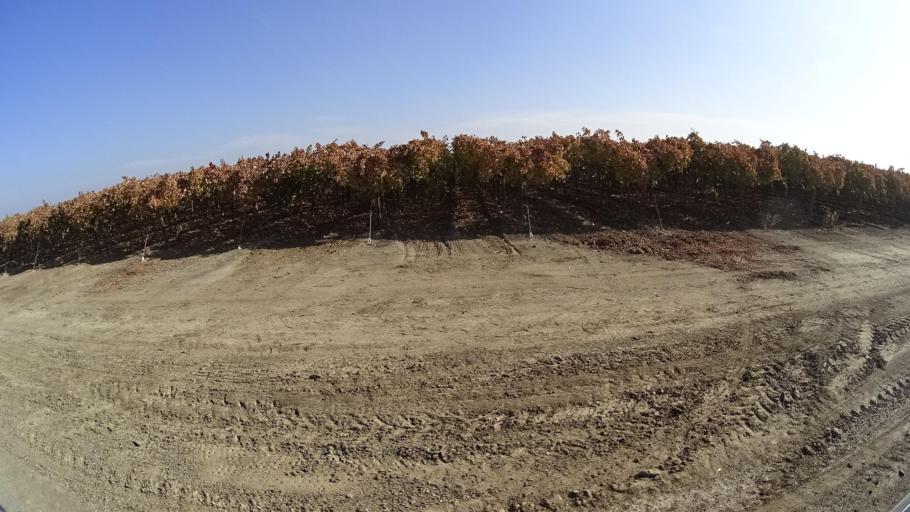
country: US
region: California
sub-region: Kern County
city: McFarland
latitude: 35.6247
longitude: -119.1866
